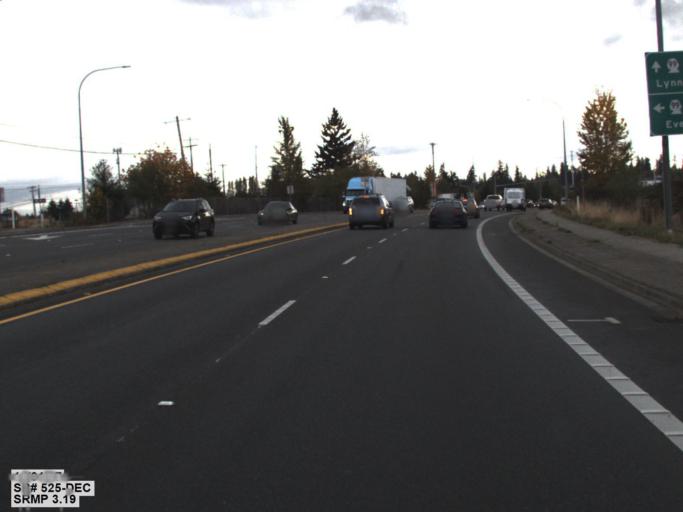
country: US
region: Washington
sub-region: Snohomish County
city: Martha Lake
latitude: 47.8755
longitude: -122.2763
